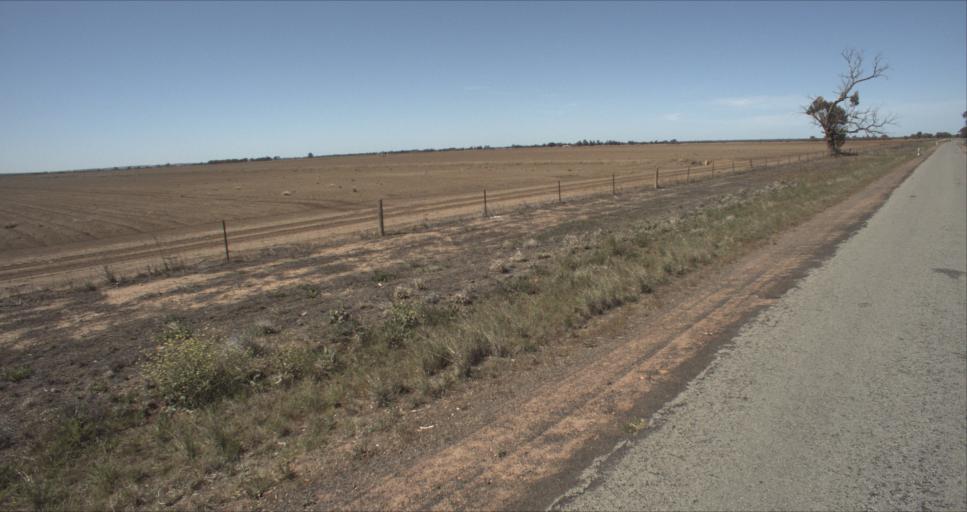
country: AU
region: New South Wales
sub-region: Leeton
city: Leeton
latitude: -34.5547
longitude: 146.3139
